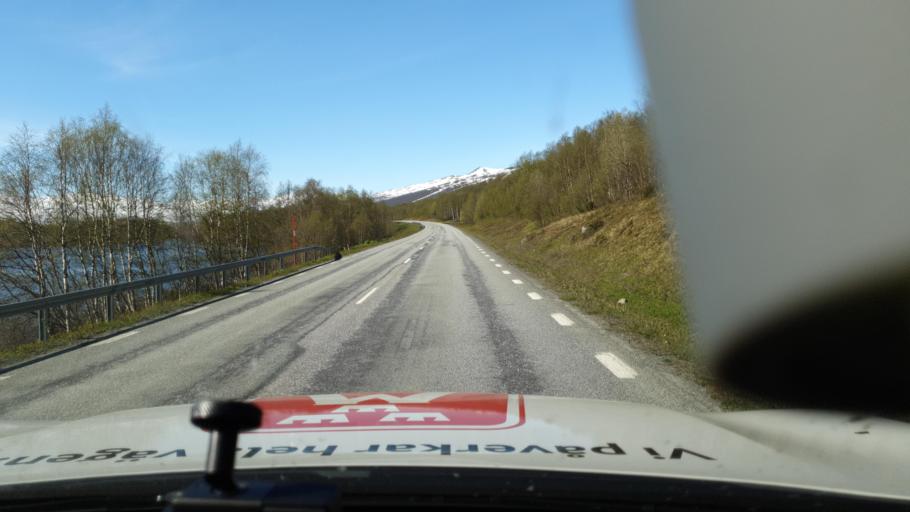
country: NO
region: Nordland
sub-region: Rana
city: Mo i Rana
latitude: 65.7887
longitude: 15.1049
